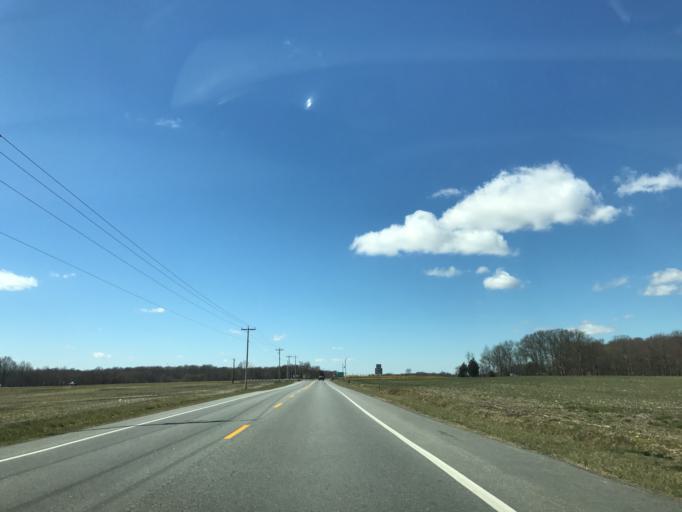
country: US
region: Maryland
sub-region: Queen Anne's County
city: Kingstown
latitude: 39.1221
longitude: -75.9391
